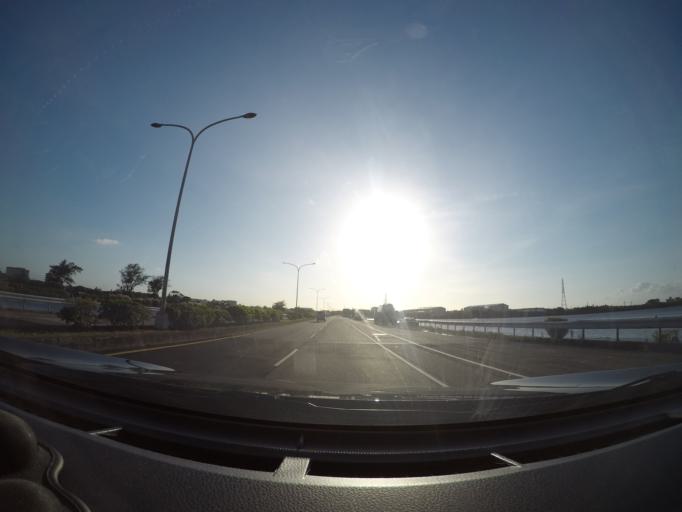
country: TW
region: Taiwan
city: Taoyuan City
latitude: 25.0758
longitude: 121.2040
